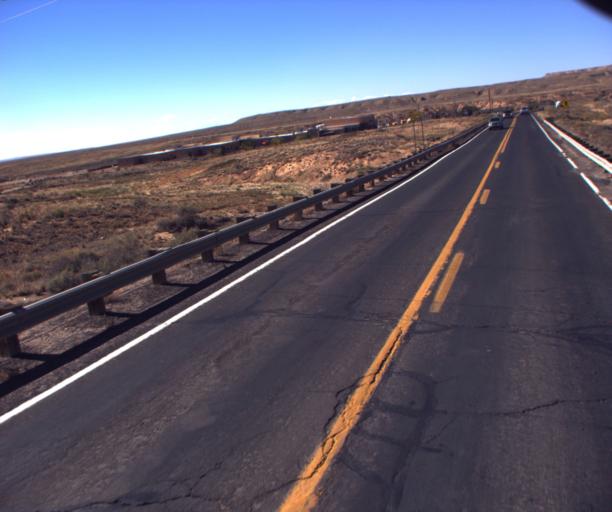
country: US
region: Arizona
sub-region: Navajo County
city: First Mesa
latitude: 35.7930
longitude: -110.5012
